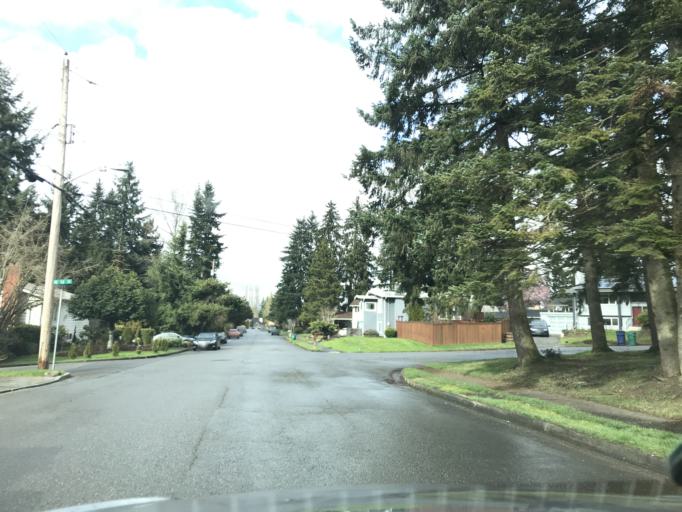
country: US
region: Washington
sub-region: King County
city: Redmond
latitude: 47.6565
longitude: -122.1340
